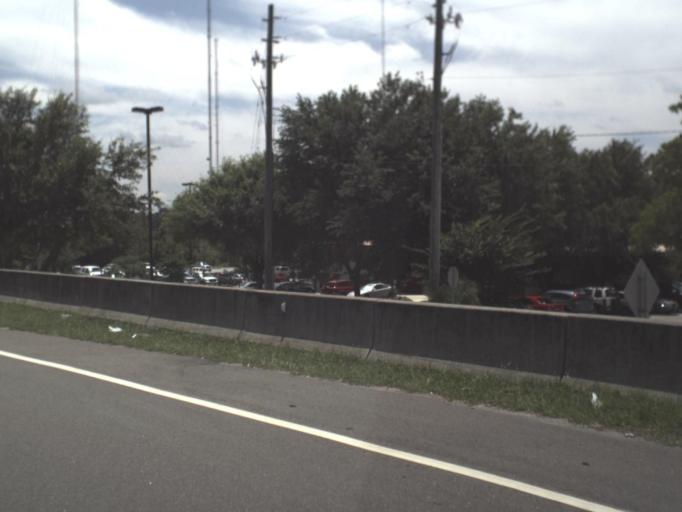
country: US
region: Florida
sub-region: Duval County
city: Jacksonville
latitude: 30.2834
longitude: -81.5593
